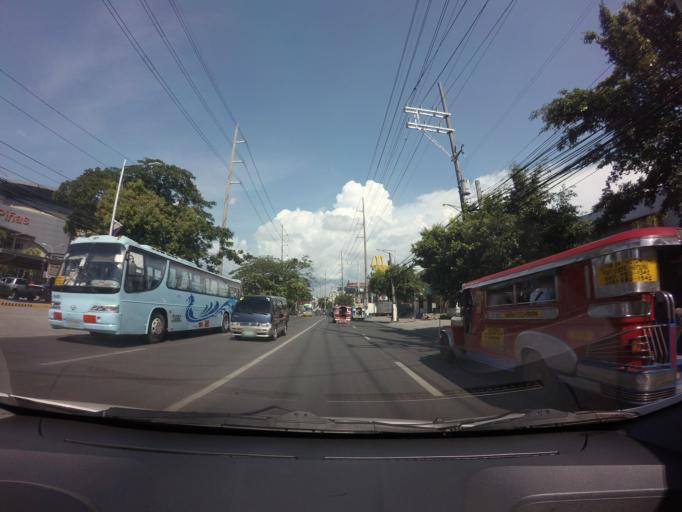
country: PH
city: Sambayanihan People's Village
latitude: 14.4421
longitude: 120.9975
